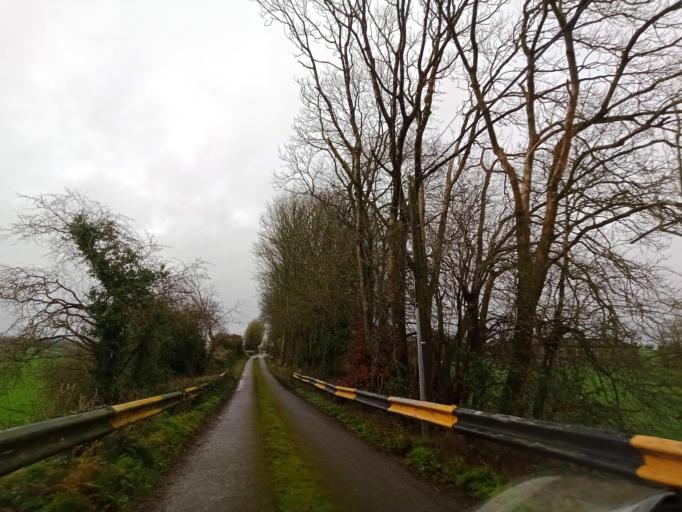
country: IE
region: Munster
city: Fethard
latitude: 52.5592
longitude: -7.7083
